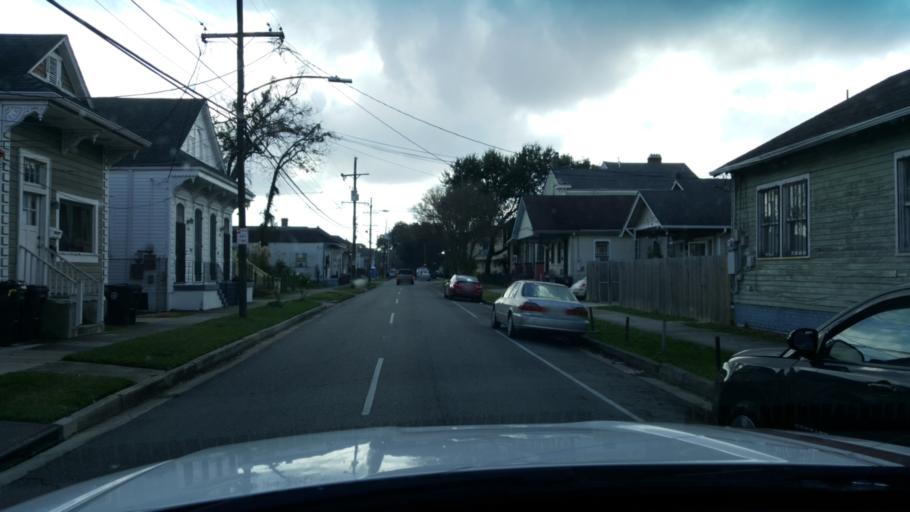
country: US
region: Louisiana
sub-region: Orleans Parish
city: New Orleans
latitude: 29.9764
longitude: -90.0710
